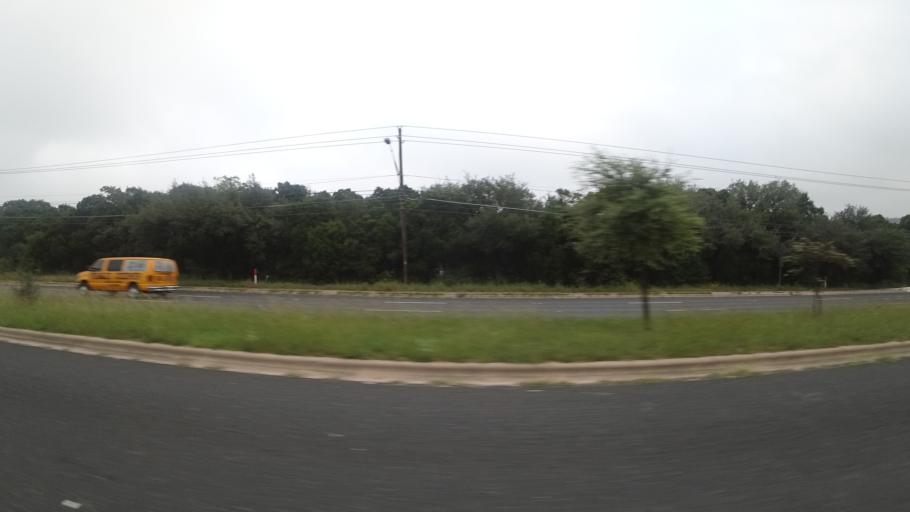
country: US
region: Texas
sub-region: Travis County
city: Wells Branch
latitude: 30.3664
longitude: -97.6689
